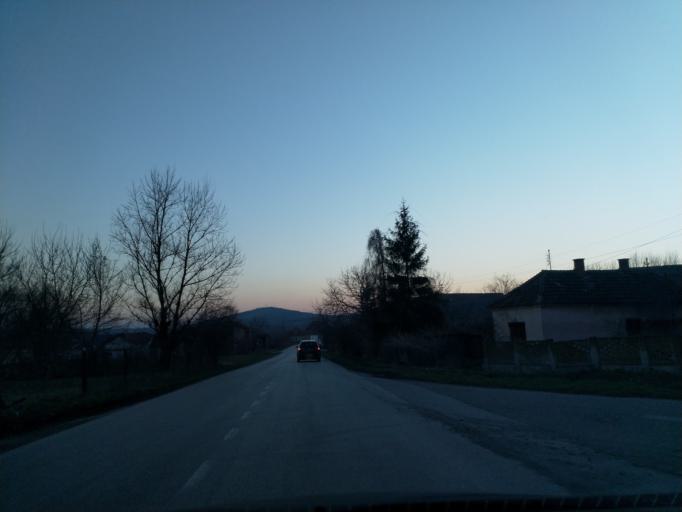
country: RS
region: Central Serbia
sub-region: Pomoravski Okrug
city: Paracin
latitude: 43.8856
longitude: 21.4808
